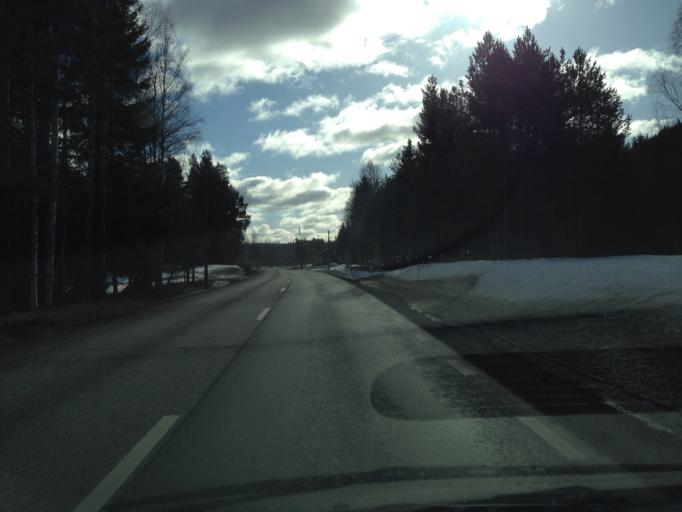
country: SE
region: Gaevleborg
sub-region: Ljusdals Kommun
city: Farila
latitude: 61.9783
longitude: 15.3258
